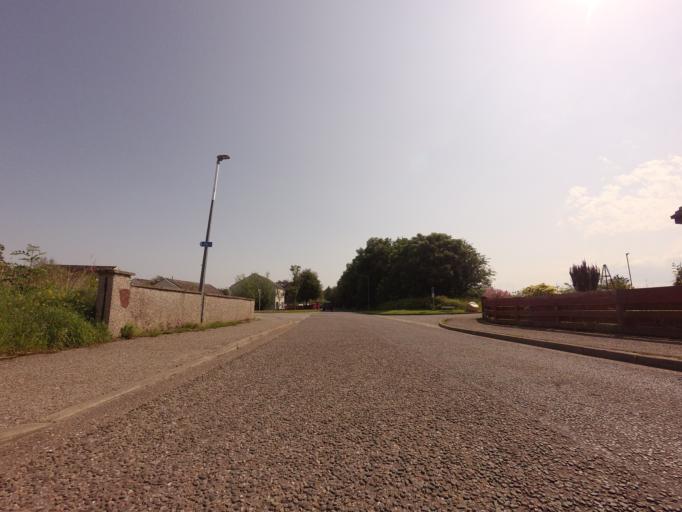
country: GB
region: Scotland
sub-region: Highland
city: Tain
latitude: 57.8052
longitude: -4.0580
